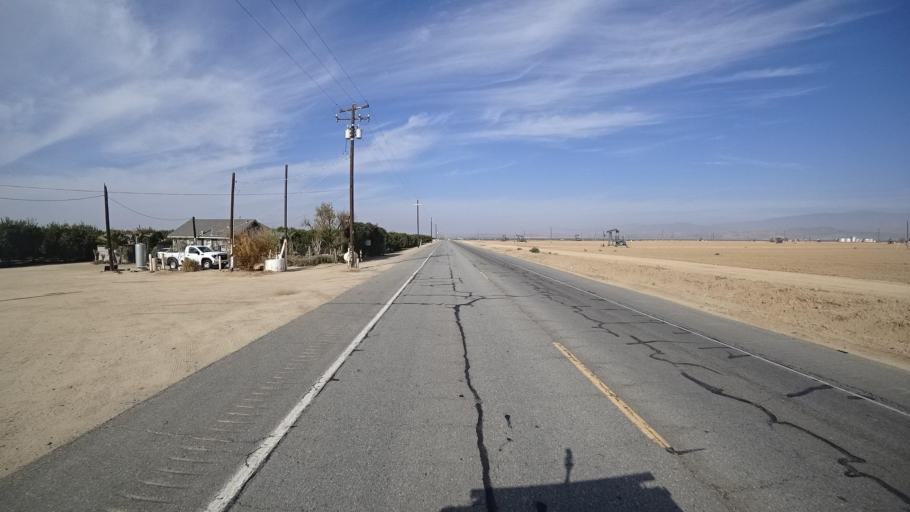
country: US
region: California
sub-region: Kern County
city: Lamont
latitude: 35.3196
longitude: -118.8431
